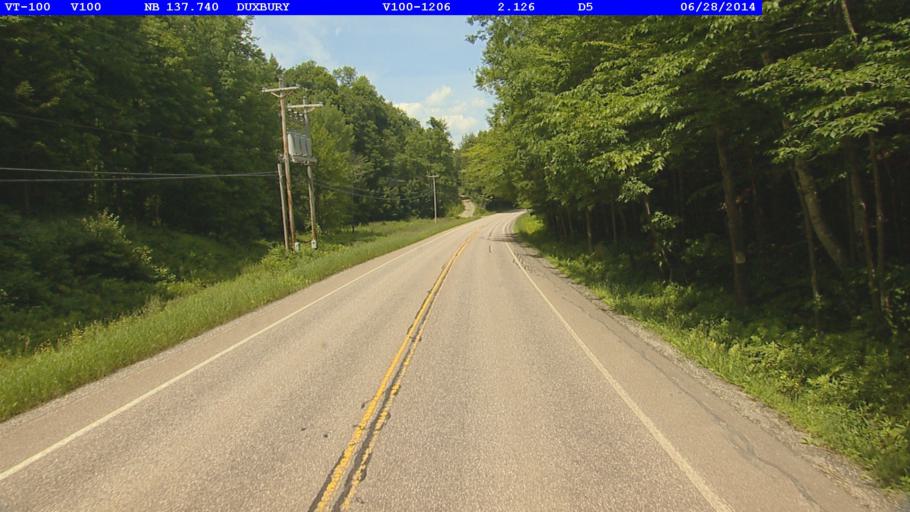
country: US
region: Vermont
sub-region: Washington County
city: Waterbury
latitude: 44.2763
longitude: -72.7845
